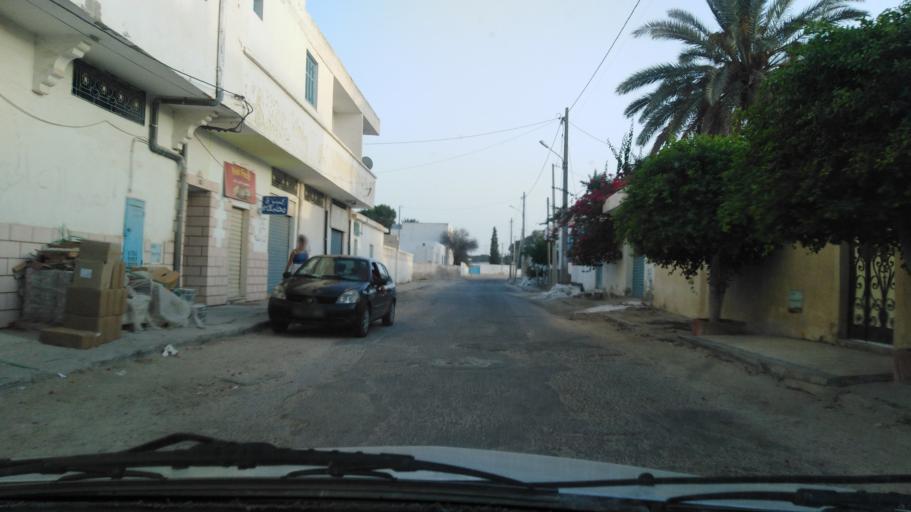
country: TN
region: Qabis
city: Gabes
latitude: 33.9587
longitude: 10.0020
